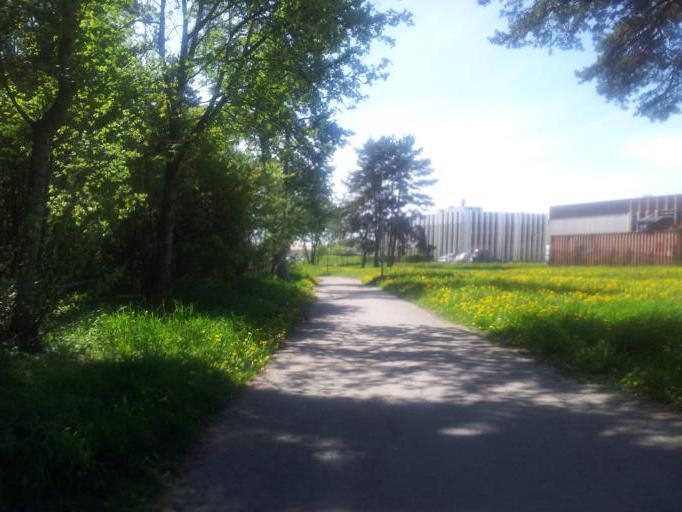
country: SE
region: Uppsala
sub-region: Uppsala Kommun
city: Saevja
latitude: 59.8593
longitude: 17.6972
